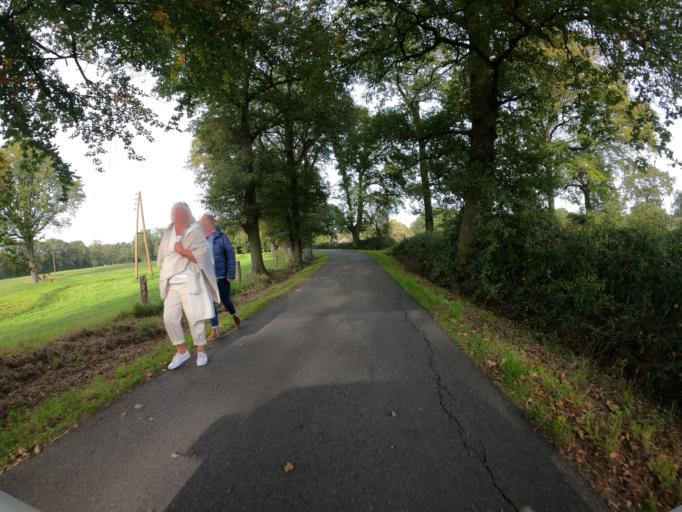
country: DE
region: North Rhine-Westphalia
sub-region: Regierungsbezirk Dusseldorf
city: Schermbeck
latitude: 51.6947
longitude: 6.8577
